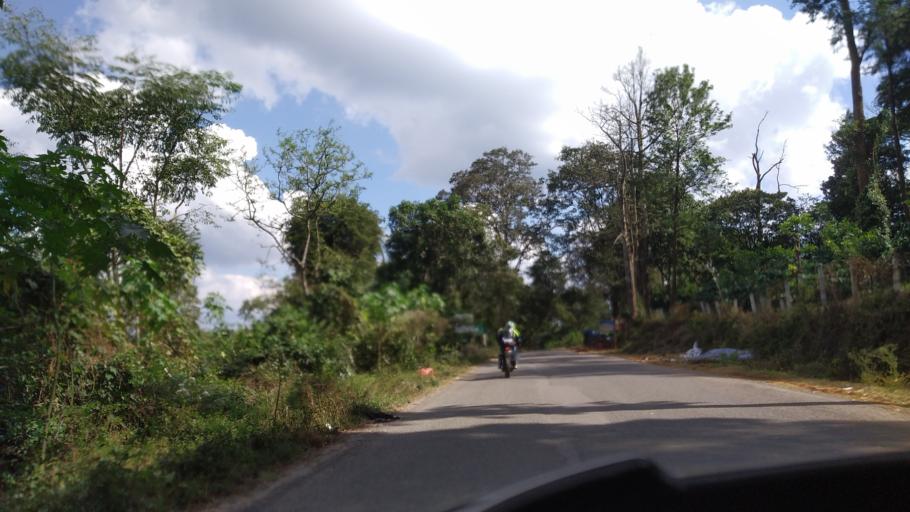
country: IN
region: Karnataka
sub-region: Kodagu
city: Ponnampet
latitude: 11.9604
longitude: 76.0613
